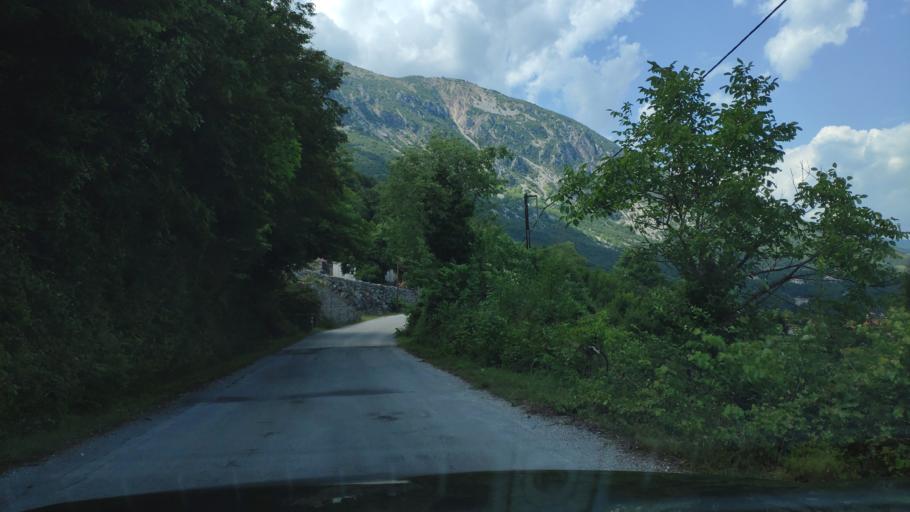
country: GR
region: Epirus
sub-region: Nomos Artas
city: Agios Dimitrios
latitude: 39.4332
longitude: 21.0161
